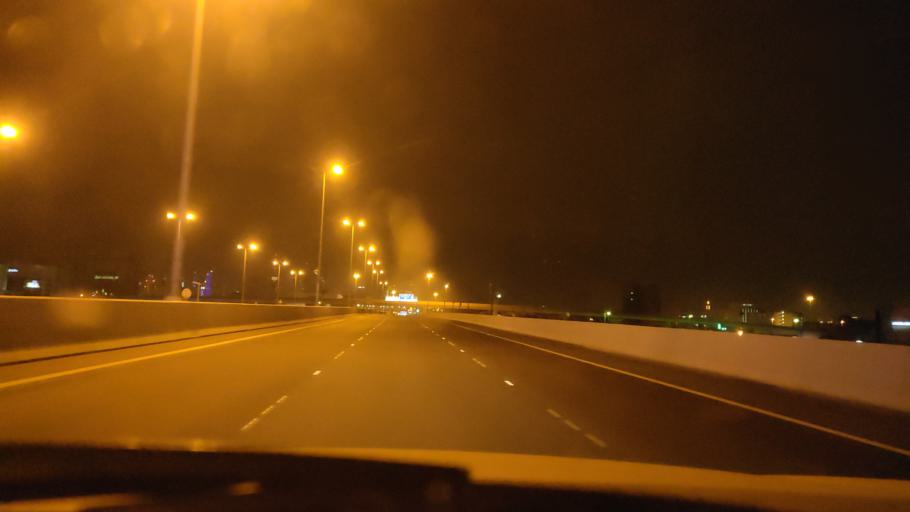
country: KW
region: Al Asimah
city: Ash Shamiyah
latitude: 29.3386
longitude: 47.9418
